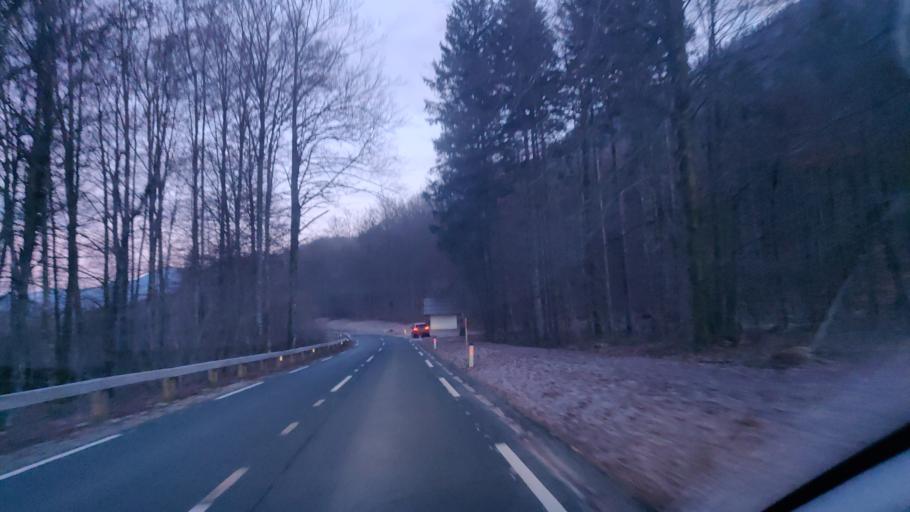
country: SI
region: Bohinj
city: Bohinjska Bistrica
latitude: 46.2812
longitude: 13.8518
